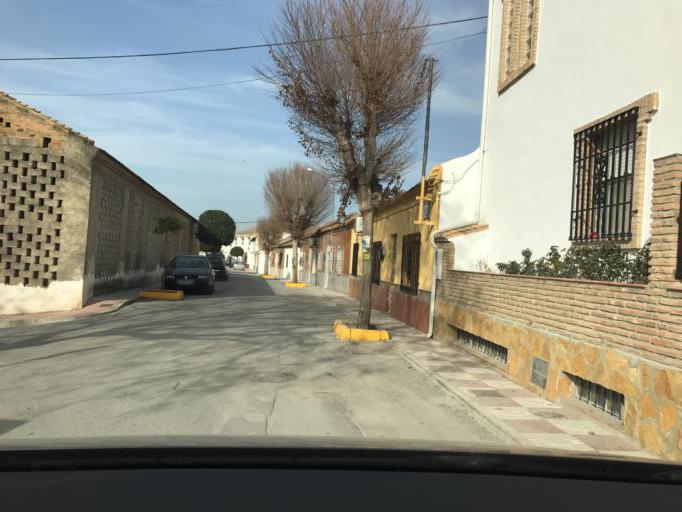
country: ES
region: Andalusia
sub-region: Provincia de Granada
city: Cullar-Vega
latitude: 37.1628
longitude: -3.6604
